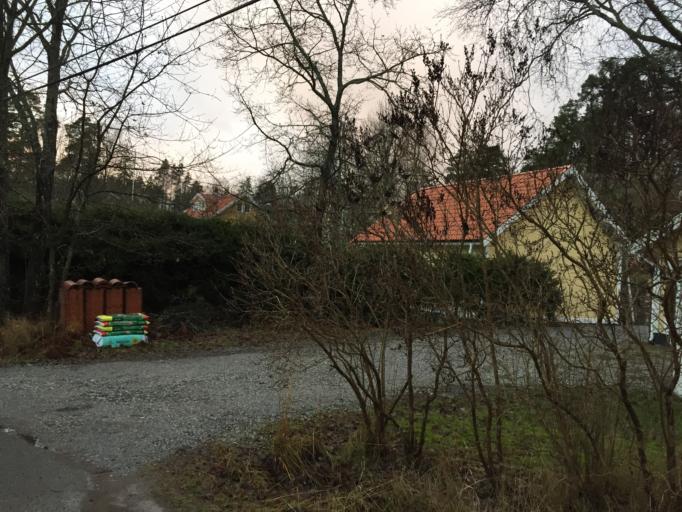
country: SE
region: Stockholm
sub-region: Salems Kommun
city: Ronninge
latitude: 59.1898
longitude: 17.7531
